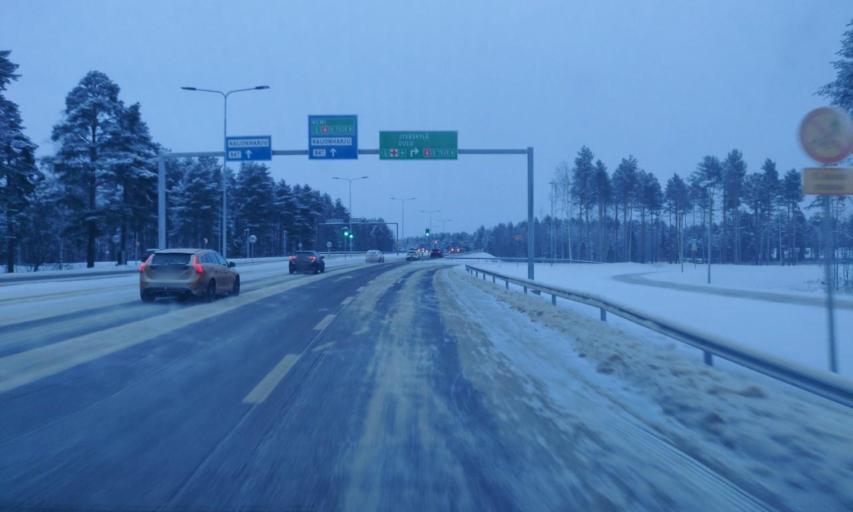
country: FI
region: Northern Ostrobothnia
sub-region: Oulu
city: Oulu
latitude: 65.0394
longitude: 25.4705
